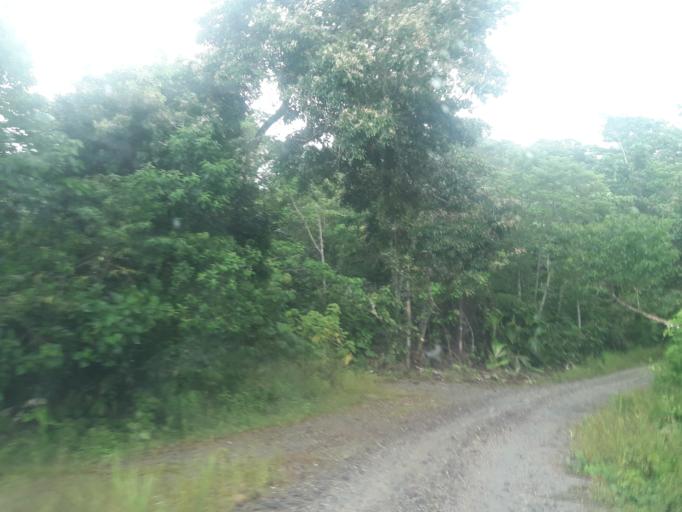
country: EC
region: Napo
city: Tena
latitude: -1.0911
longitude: -77.7047
